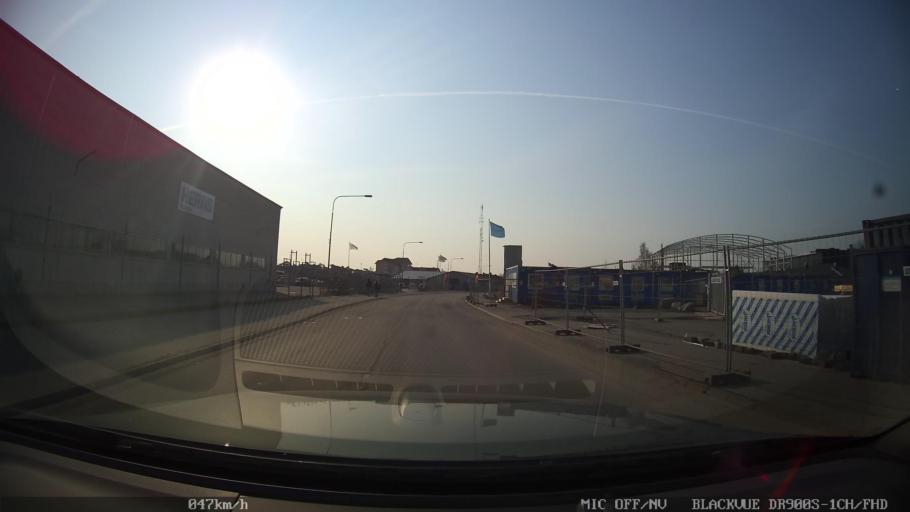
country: SE
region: Skane
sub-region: Ystads Kommun
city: Ystad
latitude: 55.4358
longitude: 13.8334
